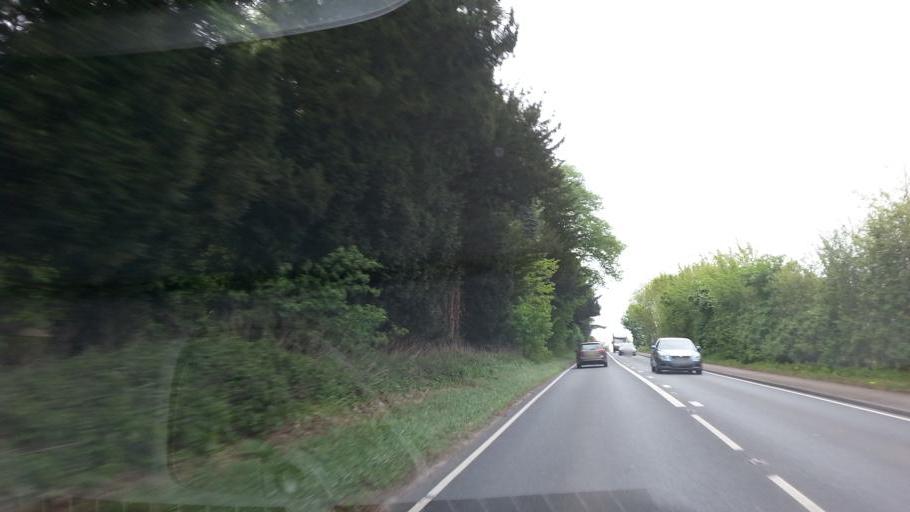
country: GB
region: England
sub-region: Suffolk
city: Bury St Edmunds
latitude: 52.2227
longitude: 0.7373
